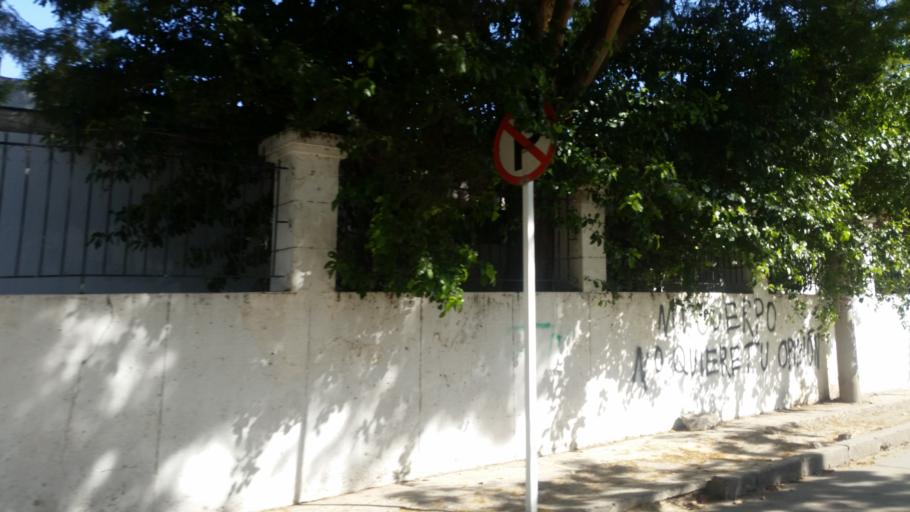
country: CO
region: Magdalena
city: Santa Marta
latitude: 11.2366
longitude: -74.2109
